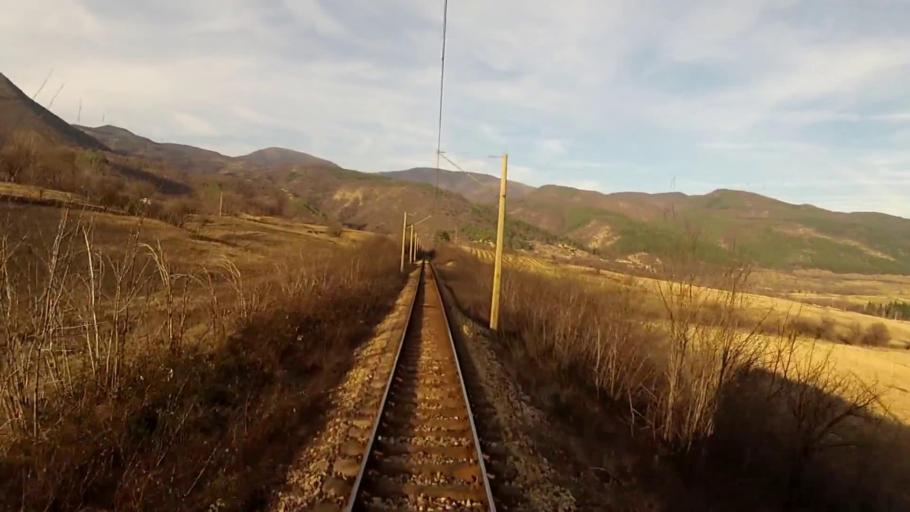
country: BG
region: Plovdiv
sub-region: Obshtina Karlovo
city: Klisura
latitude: 42.7144
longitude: 24.5533
